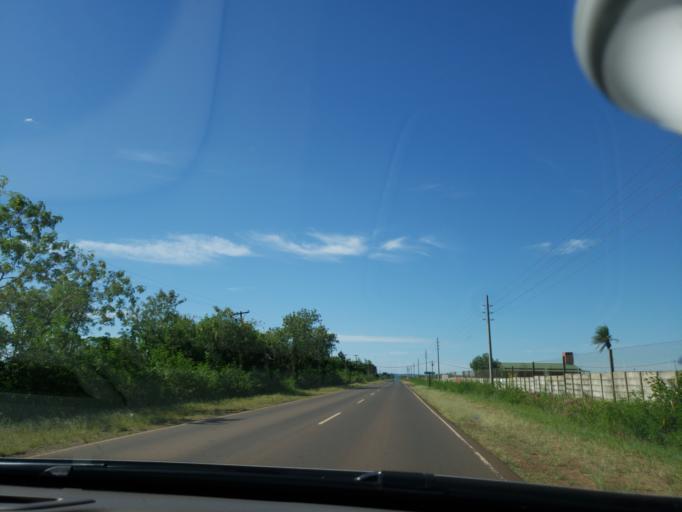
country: AR
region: Misiones
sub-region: Departamento de Capital
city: Posadas
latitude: -27.3923
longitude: -55.9756
